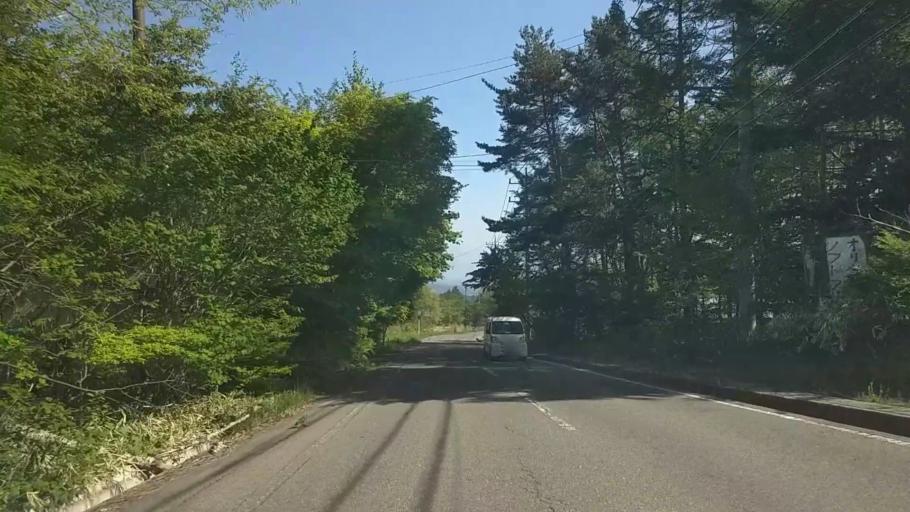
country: JP
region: Yamanashi
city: Nirasaki
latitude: 35.9045
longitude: 138.4088
